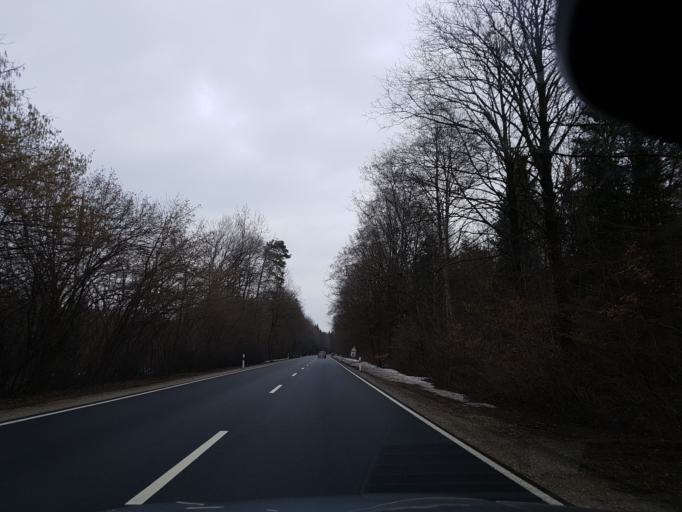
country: DE
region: Bavaria
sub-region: Upper Bavaria
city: Hohenkirchen-Siegertsbrunn
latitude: 47.9838
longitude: 11.7254
